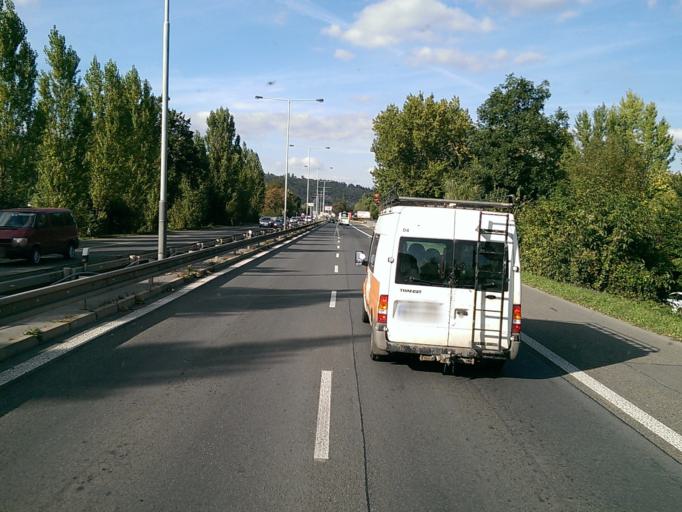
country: CZ
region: Praha
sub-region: Praha 12
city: Modrany
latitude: 50.0079
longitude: 14.3949
